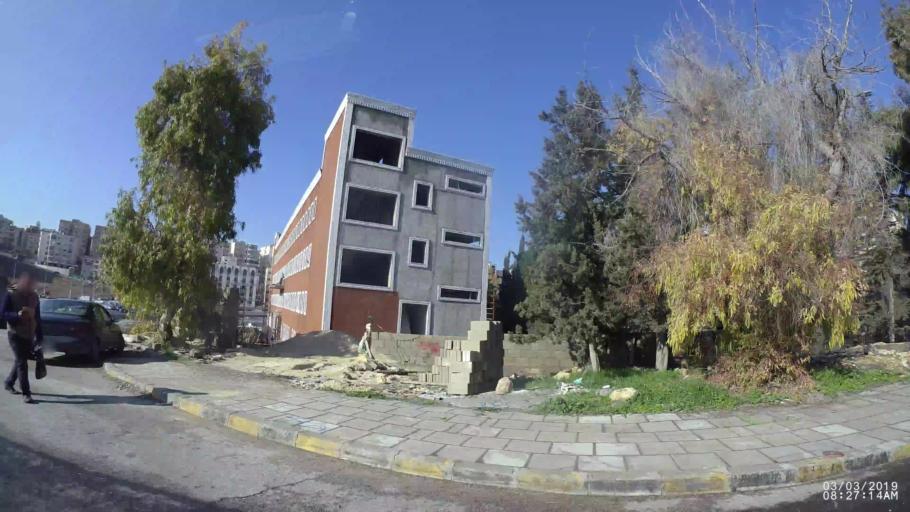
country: JO
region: Amman
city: Al Jubayhah
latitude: 31.9942
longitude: 35.8907
